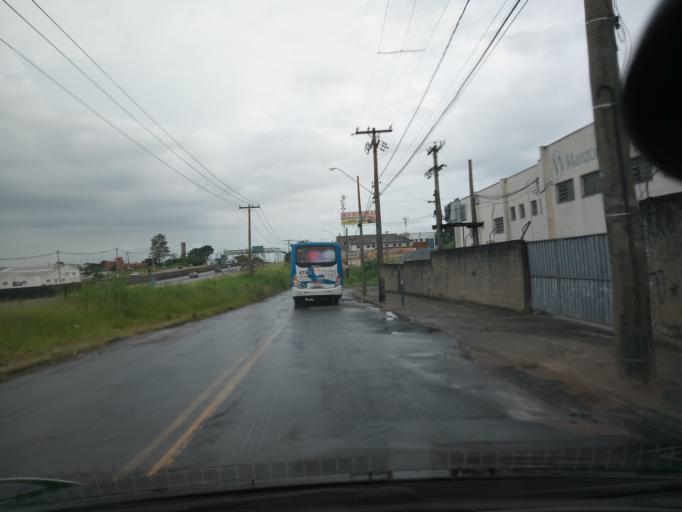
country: BR
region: Sao Paulo
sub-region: Campinas
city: Campinas
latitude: -22.9844
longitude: -47.1063
